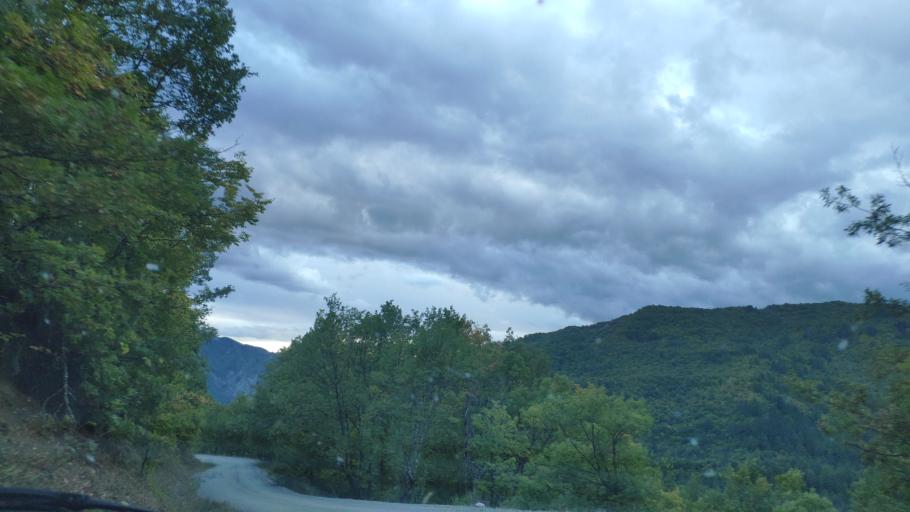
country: AL
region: Korce
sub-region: Rrethi i Kolonjes
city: Erseke
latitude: 40.2511
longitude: 20.8669
